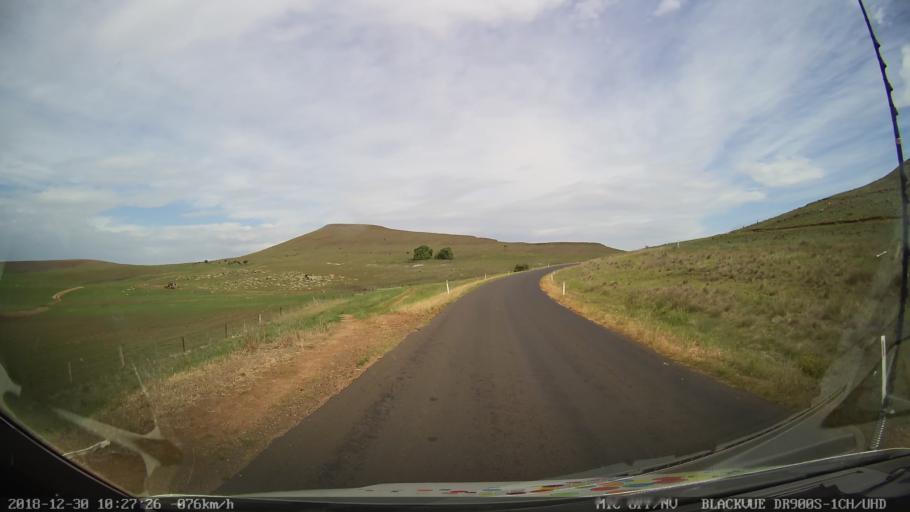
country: AU
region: New South Wales
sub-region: Snowy River
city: Berridale
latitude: -36.5138
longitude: 148.9334
